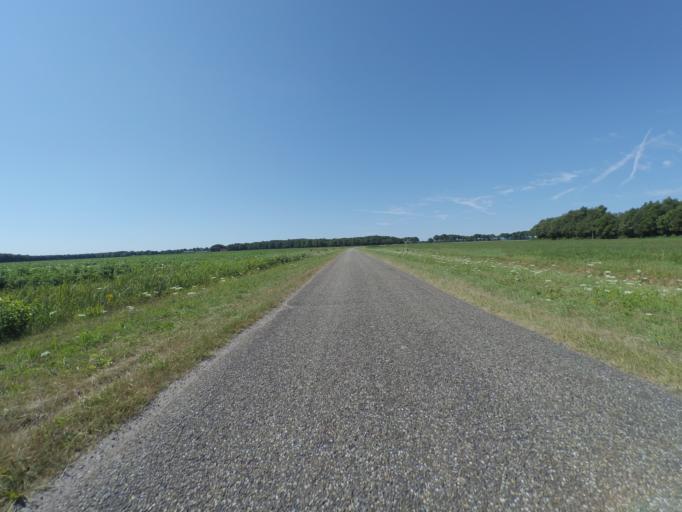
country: NL
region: Drenthe
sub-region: Gemeente Aa en Hunze
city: Anloo
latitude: 52.9644
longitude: 6.6967
